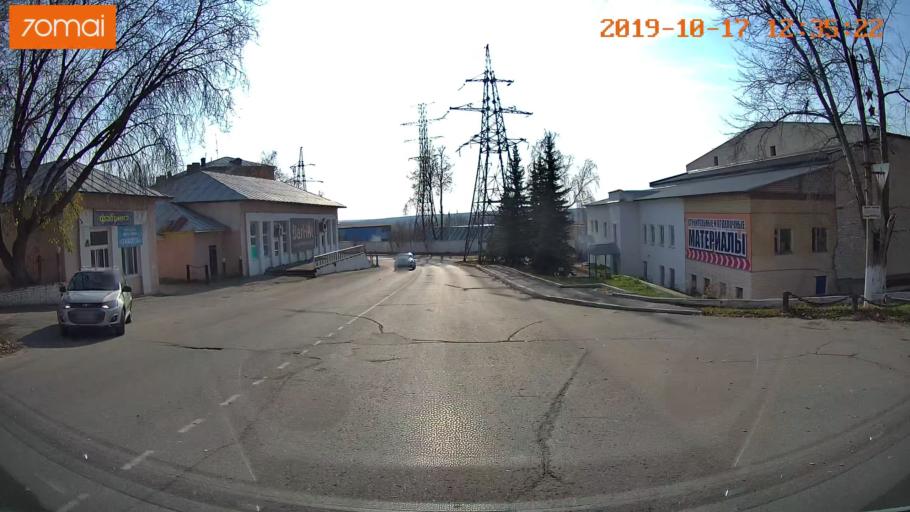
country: RU
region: Rjazan
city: Kasimov
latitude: 54.9440
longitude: 41.3698
